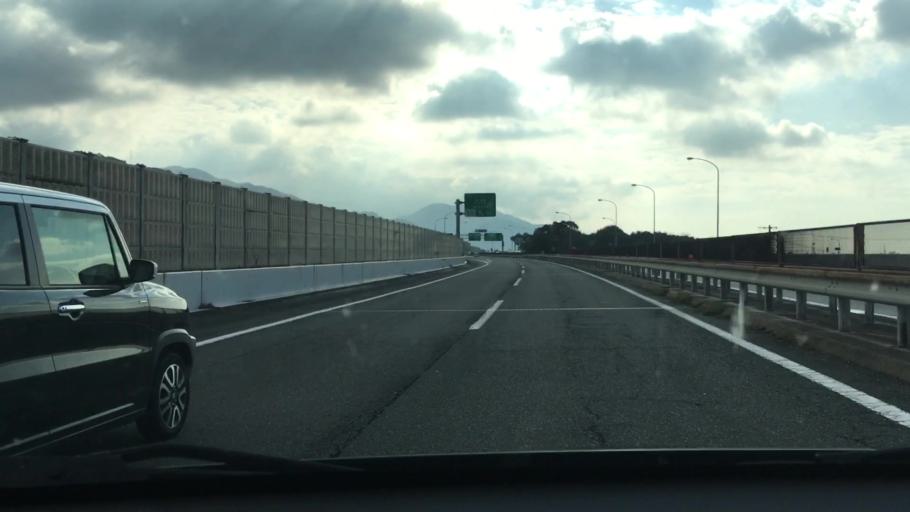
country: JP
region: Kumamoto
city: Yatsushiro
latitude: 32.5162
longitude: 130.6498
